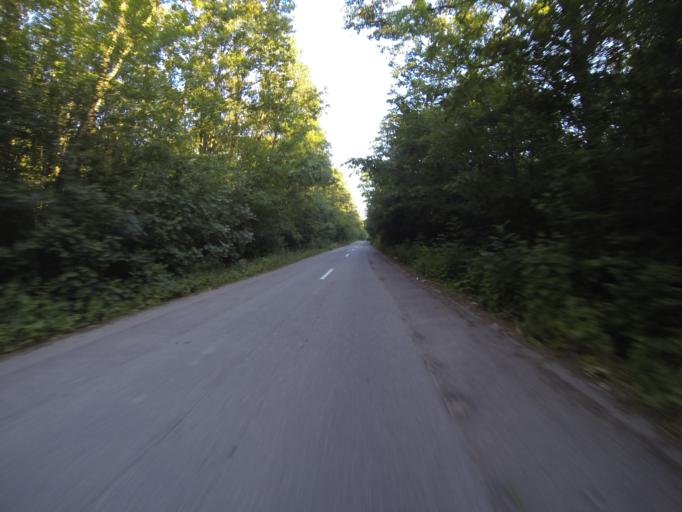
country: RO
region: Dolj
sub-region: Comuna Tuglui
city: Tuglui
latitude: 44.1674
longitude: 23.8257
